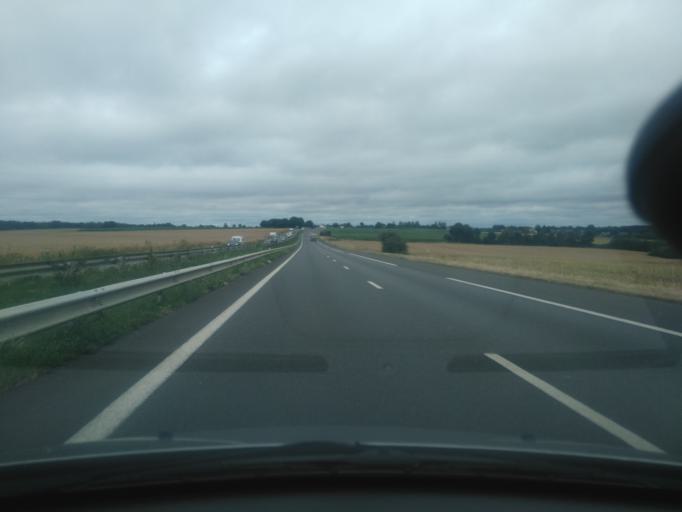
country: FR
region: Brittany
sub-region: Departement des Cotes-d'Armor
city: Plestan
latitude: 48.4360
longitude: -2.4712
